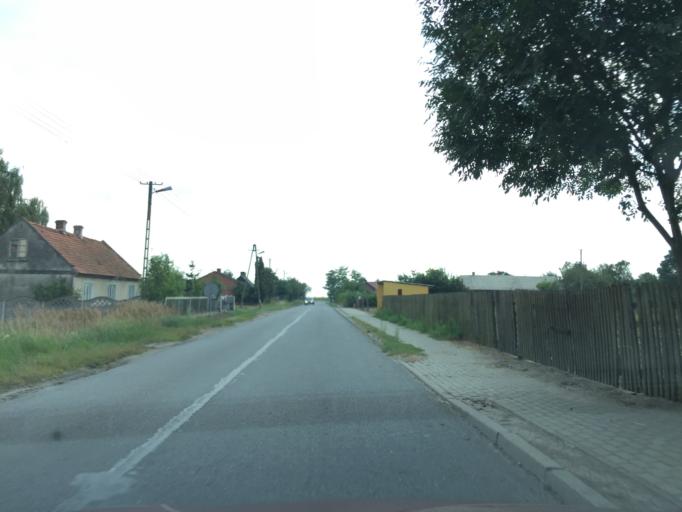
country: PL
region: Greater Poland Voivodeship
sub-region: Powiat kaliski
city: Stawiszyn
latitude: 51.9434
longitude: 18.1888
